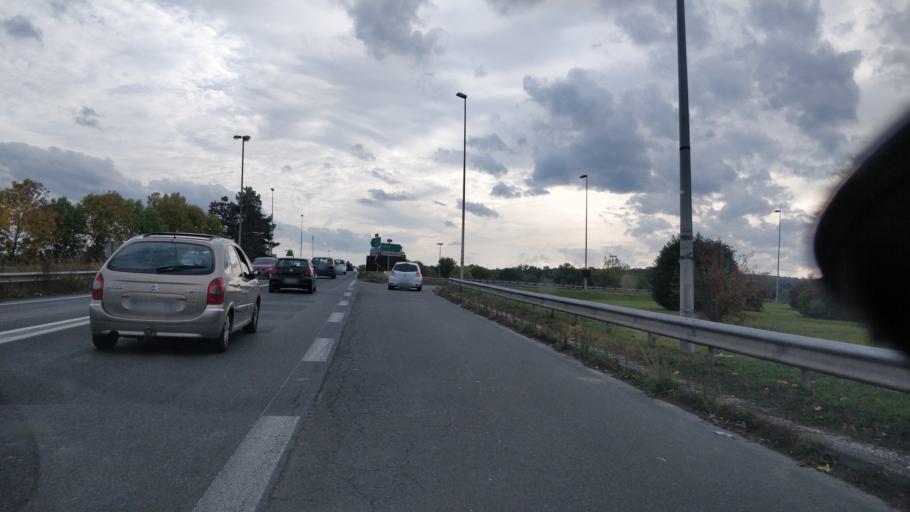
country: FR
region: Ile-de-France
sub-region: Departement de Seine-et-Marne
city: Claye-Souilly
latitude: 48.9451
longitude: 2.6671
